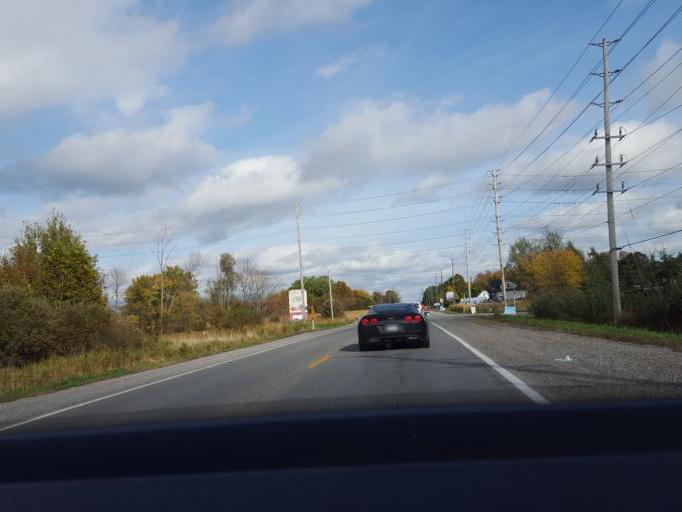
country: CA
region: Ontario
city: Oshawa
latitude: 43.9561
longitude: -78.7776
